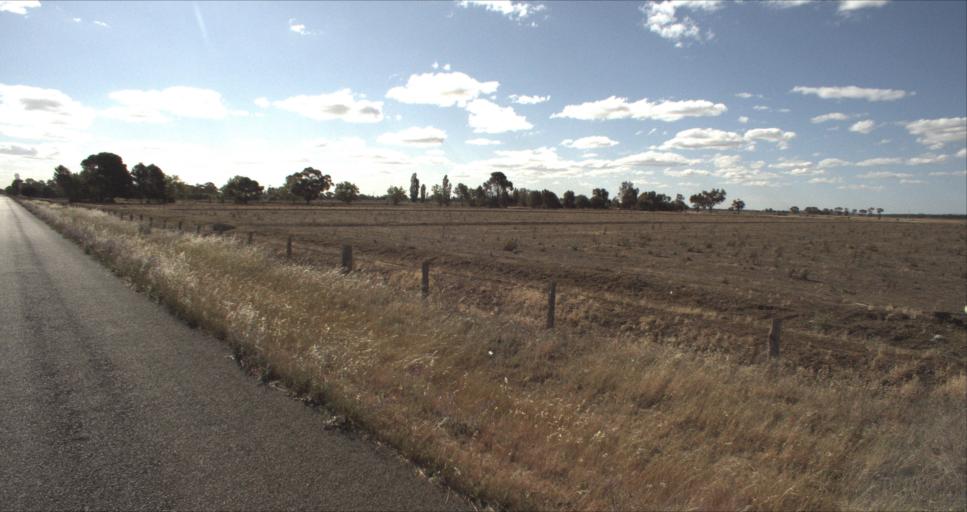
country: AU
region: New South Wales
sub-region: Leeton
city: Leeton
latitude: -34.4392
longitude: 146.2155
